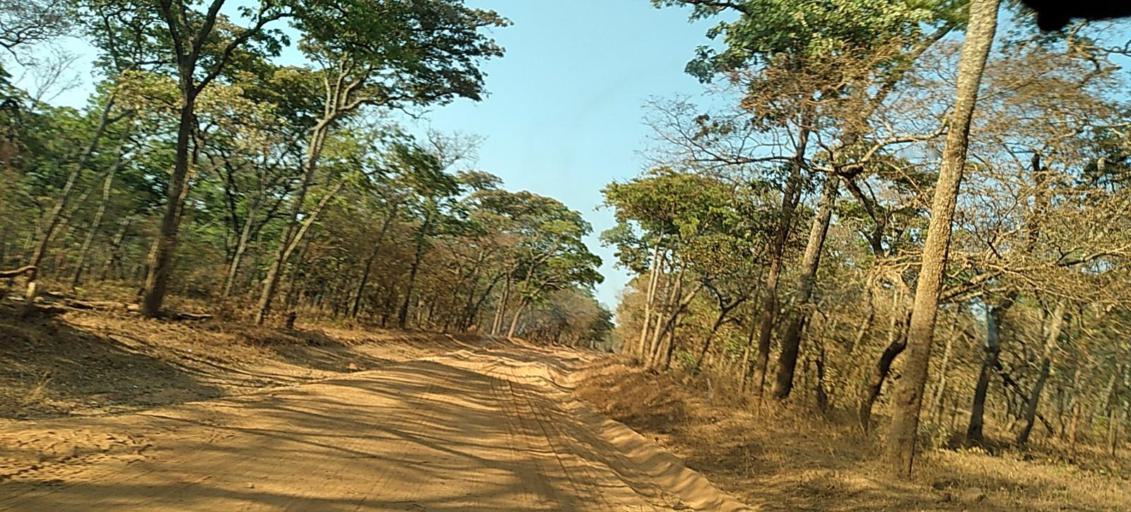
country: ZM
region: North-Western
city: Kasempa
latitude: -13.5651
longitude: 25.9968
